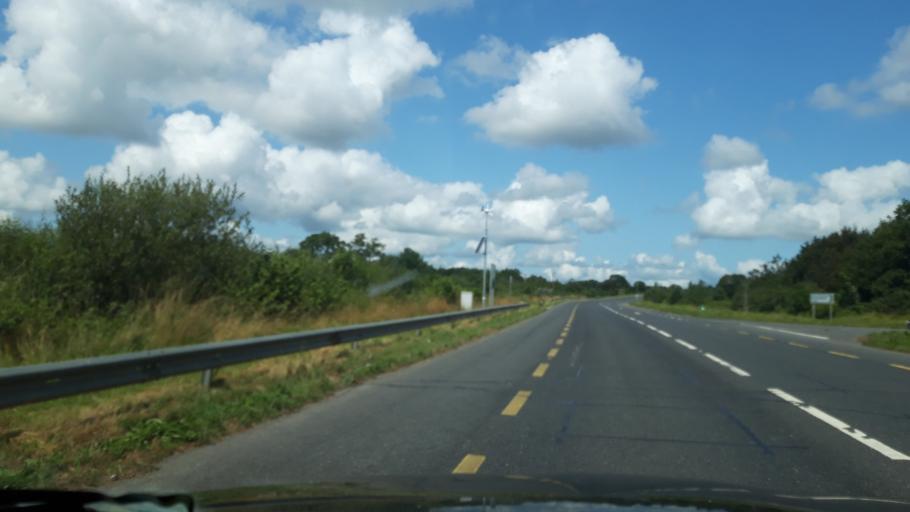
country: IE
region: Munster
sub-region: Waterford
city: Waterford
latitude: 52.2797
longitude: -7.0591
